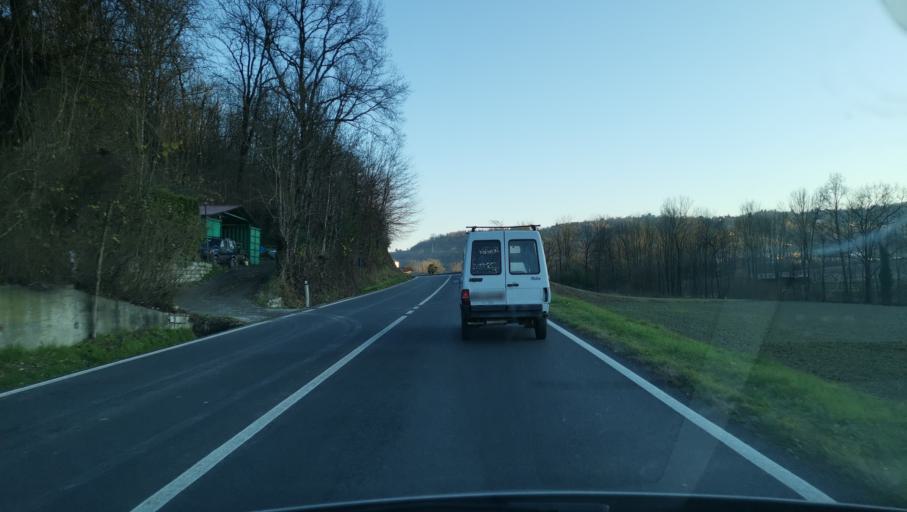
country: IT
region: Piedmont
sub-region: Provincia di Torino
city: San Raffaele Cimena
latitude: 45.1225
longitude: 7.8581
